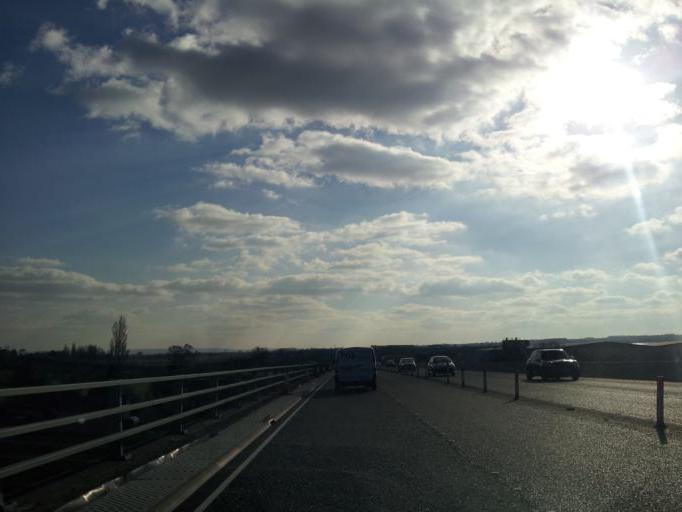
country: GB
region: England
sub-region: Somerset
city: Bridgwater
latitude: 51.1115
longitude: -2.9830
